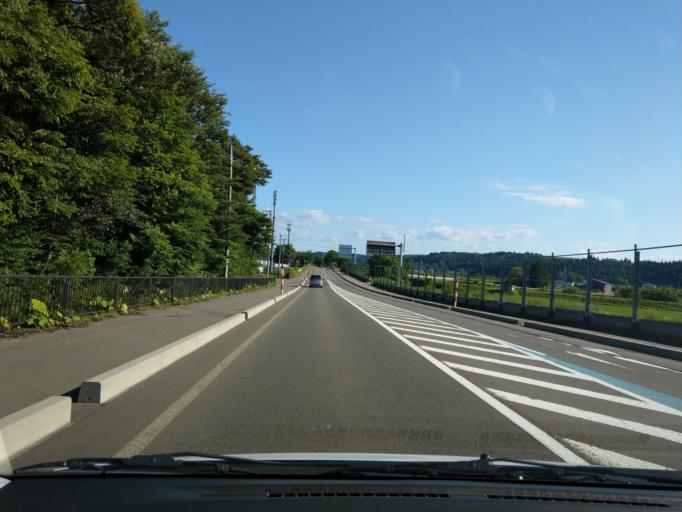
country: JP
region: Akita
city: Takanosu
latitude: 40.2008
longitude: 140.3962
